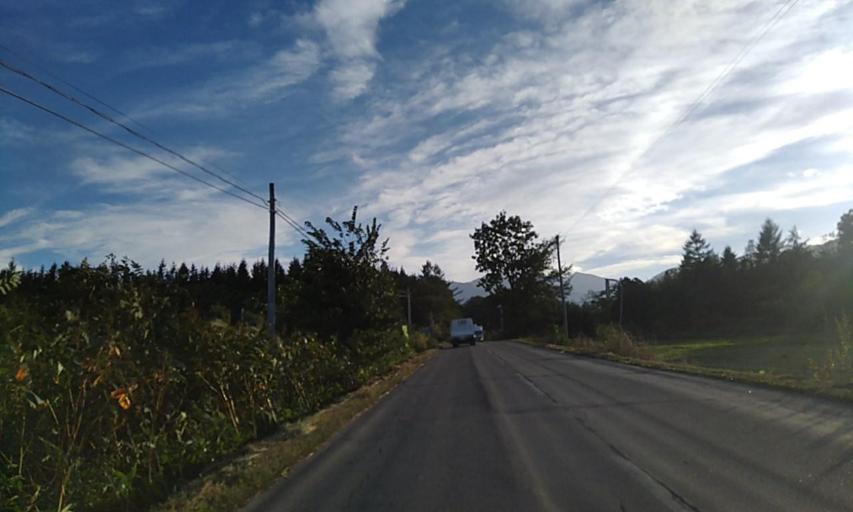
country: JP
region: Hokkaido
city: Otofuke
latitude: 42.9587
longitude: 142.9070
